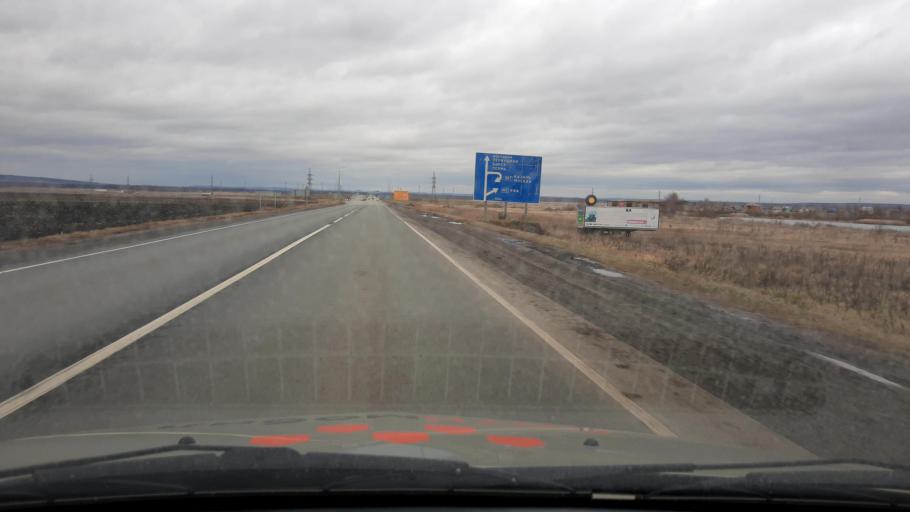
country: RU
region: Bashkortostan
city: Mikhaylovka
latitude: 54.8696
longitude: 55.7074
